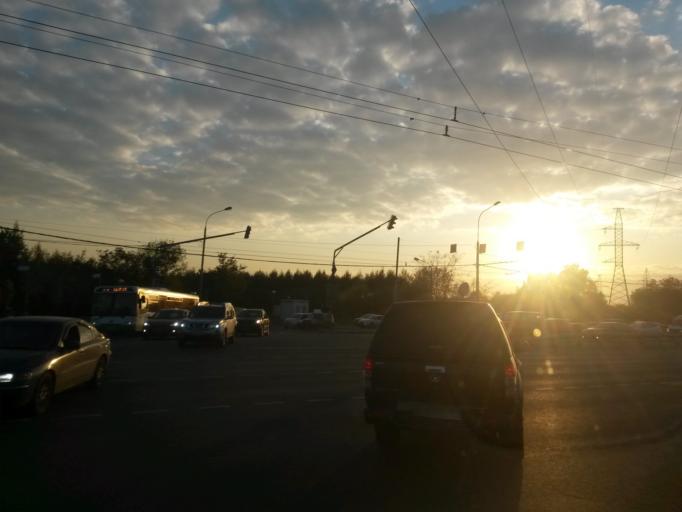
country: RU
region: Moskovskaya
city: Kur'yanovo
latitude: 55.6347
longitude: 37.7000
